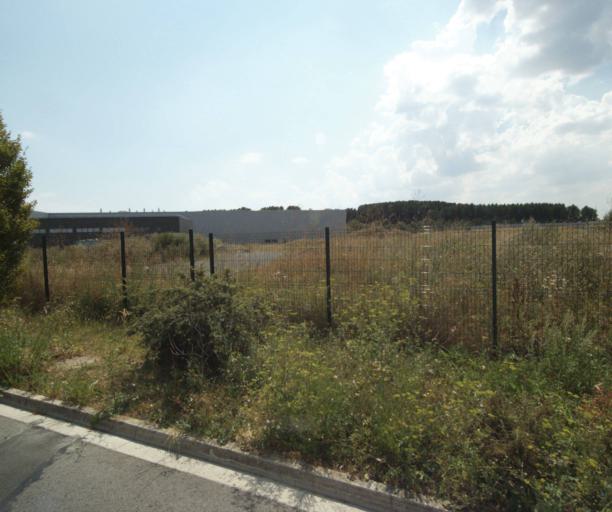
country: FR
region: Nord-Pas-de-Calais
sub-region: Departement du Nord
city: Comines
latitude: 50.7531
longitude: 2.9976
